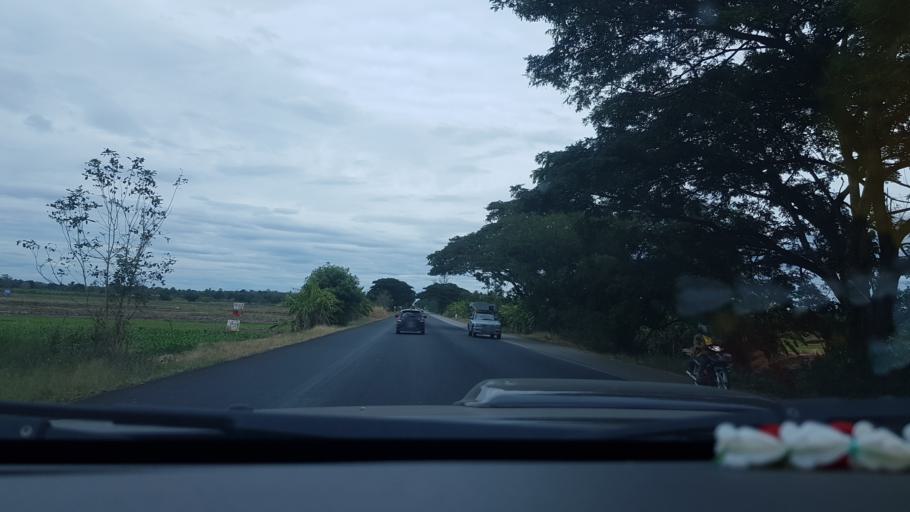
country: TH
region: Phetchabun
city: Phetchabun
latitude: 16.4564
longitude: 101.1176
